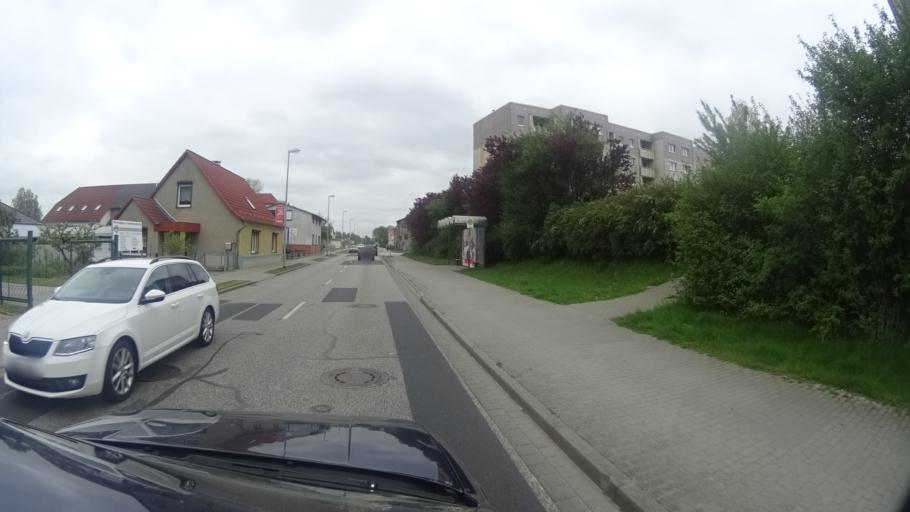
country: DE
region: Mecklenburg-Vorpommern
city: Ribnitz-Damgarten
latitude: 54.2463
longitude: 12.4130
